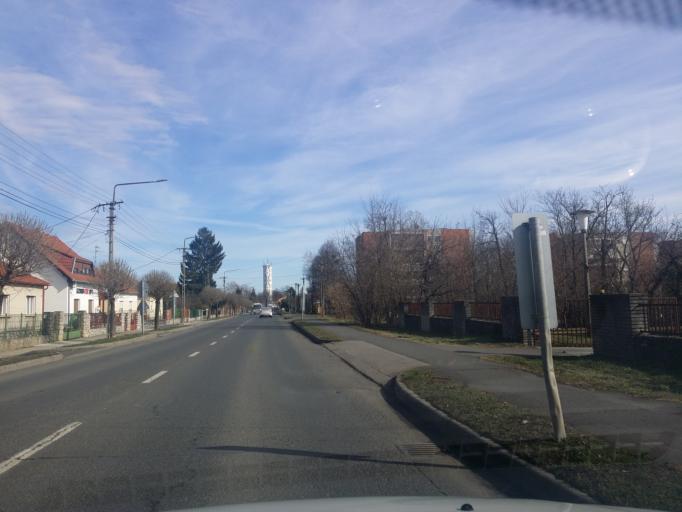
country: HU
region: Baranya
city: Mohacs
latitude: 45.9965
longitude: 18.6723
